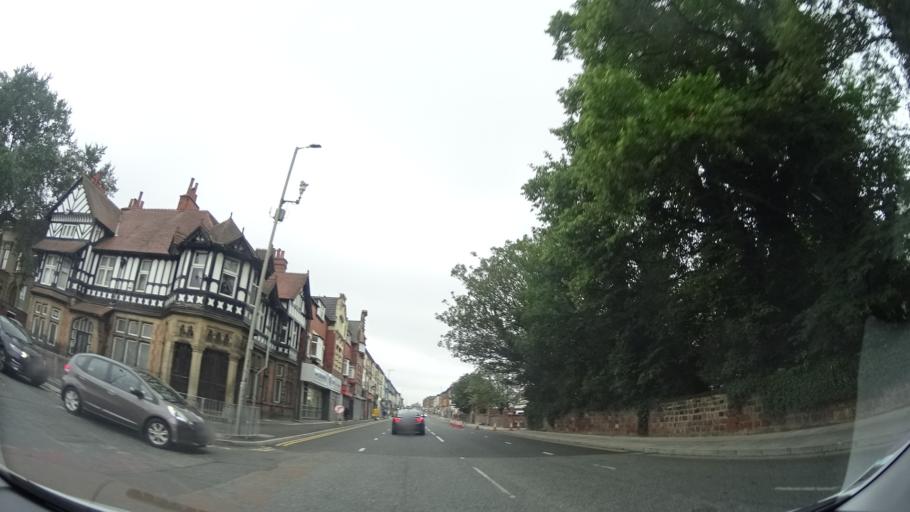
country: GB
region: England
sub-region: Liverpool
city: Liverpool
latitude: 53.4135
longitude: -2.9377
